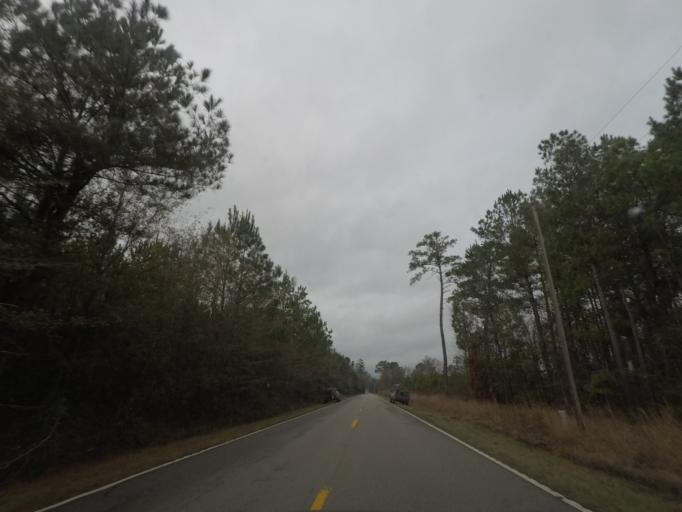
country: US
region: South Carolina
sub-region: Colleton County
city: Walterboro
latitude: 32.8755
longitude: -80.4925
